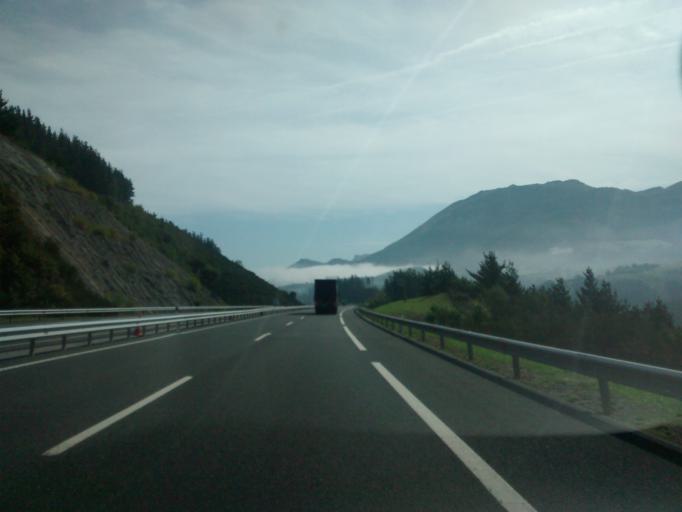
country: ES
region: Basque Country
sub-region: Provincia de Guipuzcoa
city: Eskoriatza
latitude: 43.0171
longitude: -2.5438
